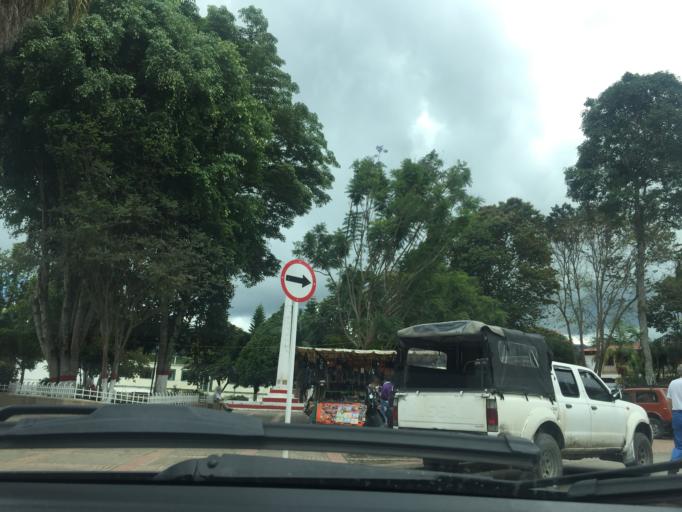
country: CO
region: Cundinamarca
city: Supata
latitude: 5.0618
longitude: -74.2365
